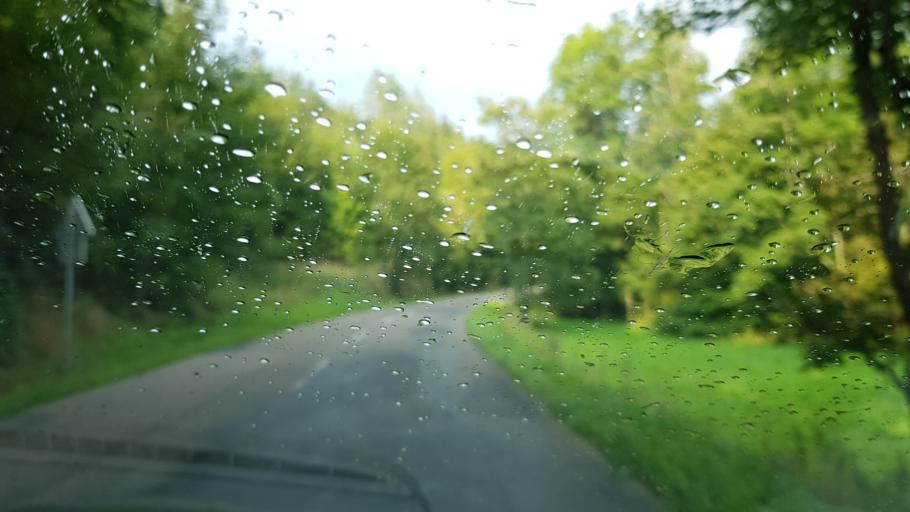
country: CZ
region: Olomoucky
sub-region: Okres Sumperk
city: Hanusovice
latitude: 50.0946
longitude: 16.8553
